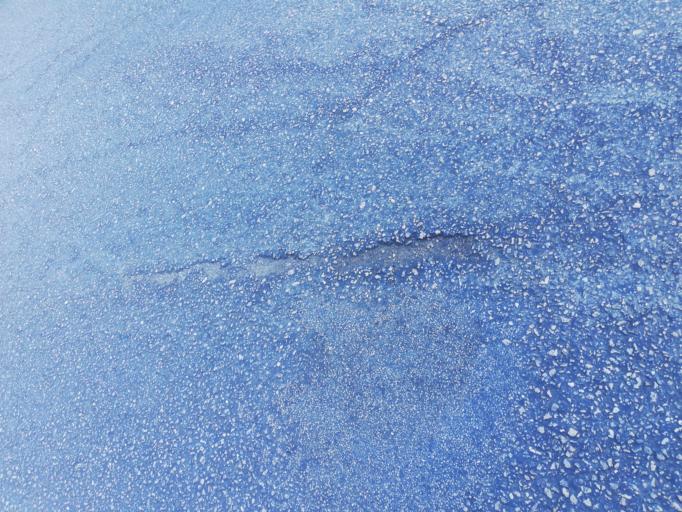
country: LB
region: Mont-Liban
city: Jdaidet el Matn
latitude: 33.8963
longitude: 35.6112
